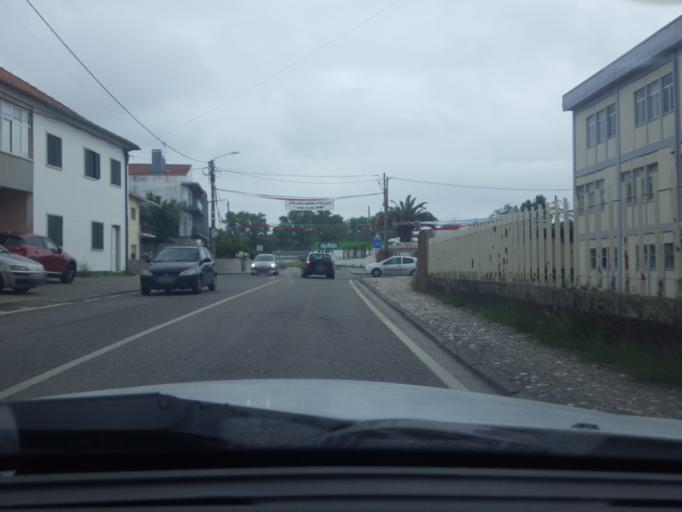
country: PT
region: Leiria
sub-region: Leiria
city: Leiria
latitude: 39.7317
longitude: -8.7946
